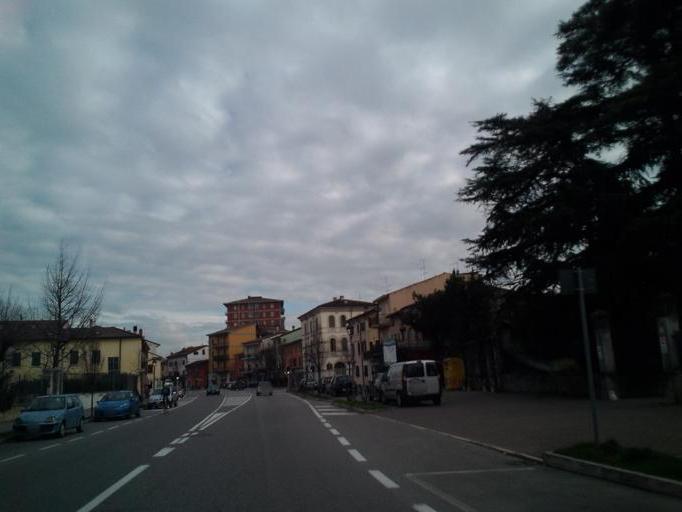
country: IT
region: Veneto
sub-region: Provincia di Verona
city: San Martino Buon Albergo
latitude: 45.4231
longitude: 11.0888
